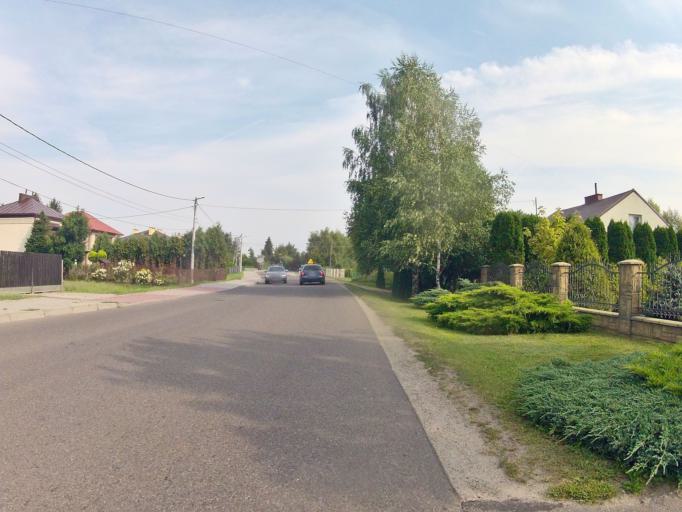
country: PL
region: Subcarpathian Voivodeship
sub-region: Powiat jasielski
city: Debowiec
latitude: 49.7133
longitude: 21.4618
